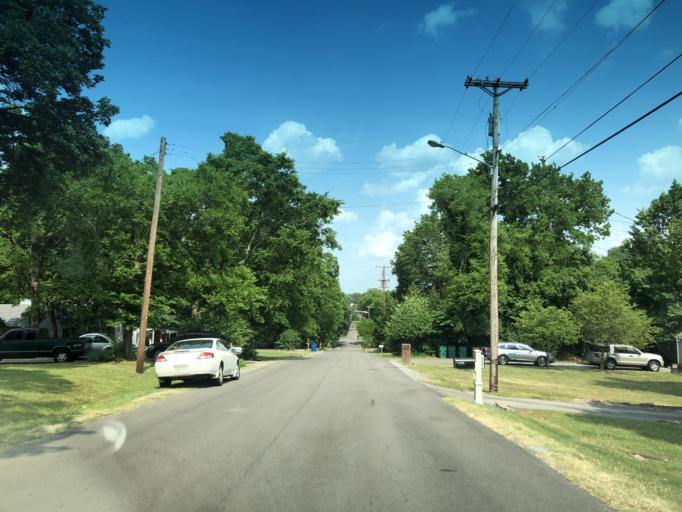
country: US
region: Tennessee
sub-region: Davidson County
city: Goodlettsville
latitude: 36.2578
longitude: -86.7310
